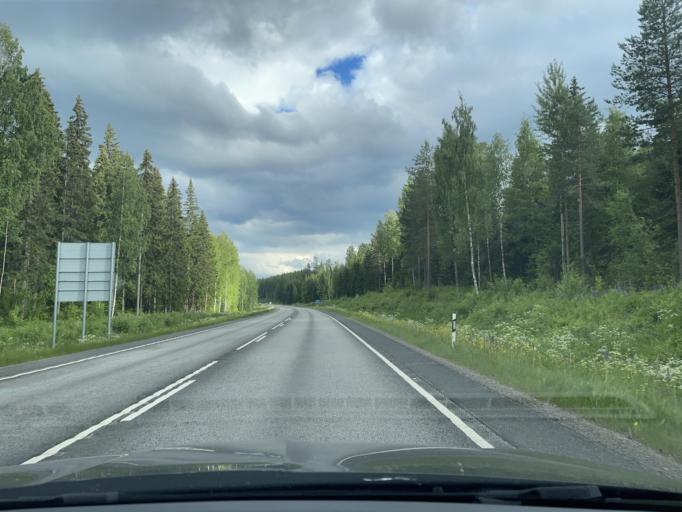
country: FI
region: Central Finland
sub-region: Jyvaeskylae
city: Jyvaeskylae
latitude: 62.2435
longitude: 25.6535
